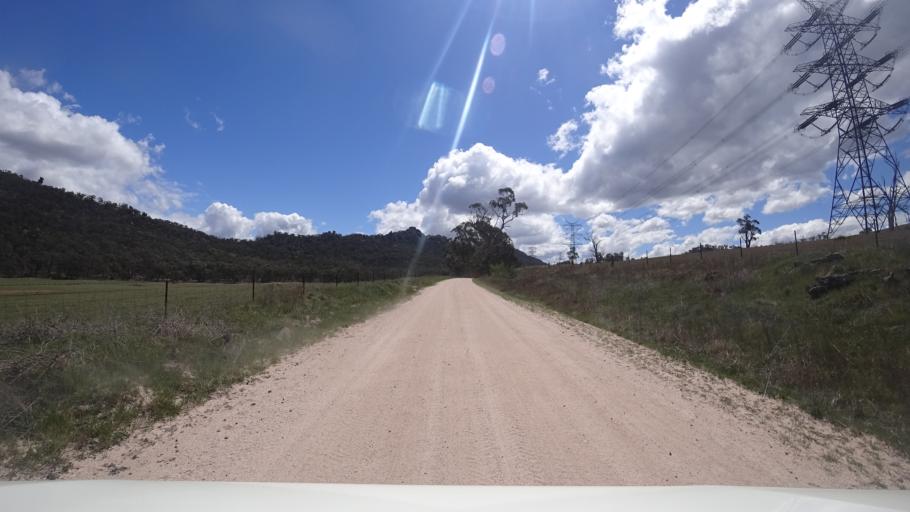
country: AU
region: New South Wales
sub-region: Oberon
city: Oberon
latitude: -33.5568
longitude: 149.9333
